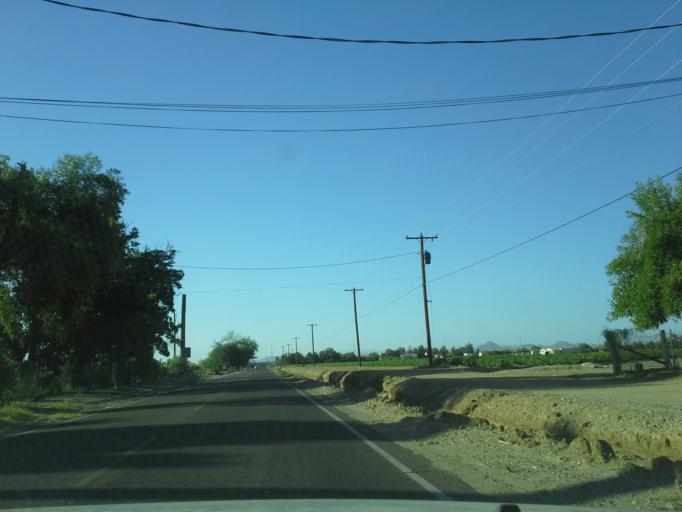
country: US
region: Arizona
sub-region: Maricopa County
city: Laveen
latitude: 33.3665
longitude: -112.1005
